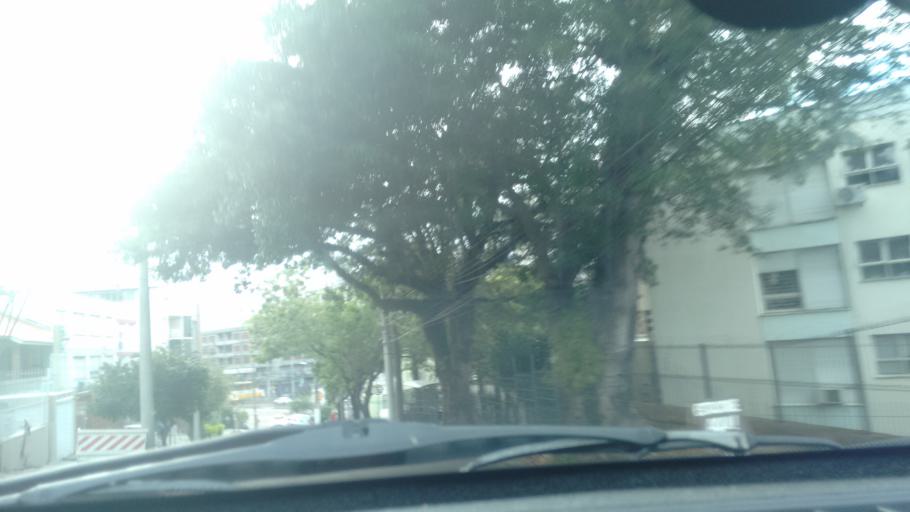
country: BR
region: Rio Grande do Sul
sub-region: Porto Alegre
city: Porto Alegre
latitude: -30.0100
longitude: -51.1614
